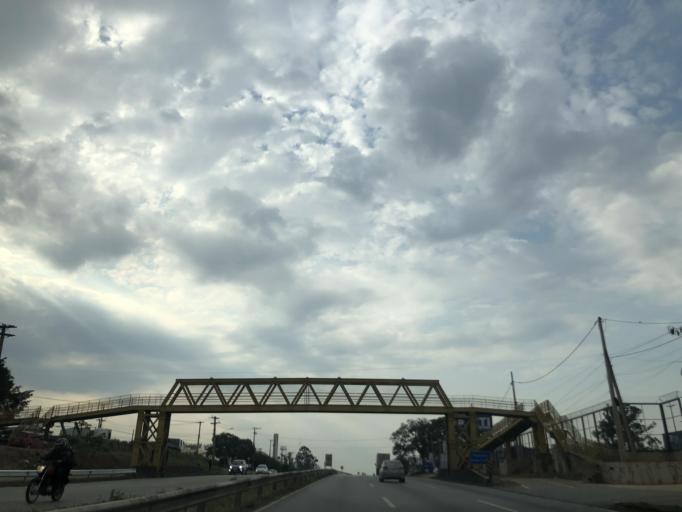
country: BR
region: Sao Paulo
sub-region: Sorocaba
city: Sorocaba
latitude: -23.5404
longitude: -47.4871
